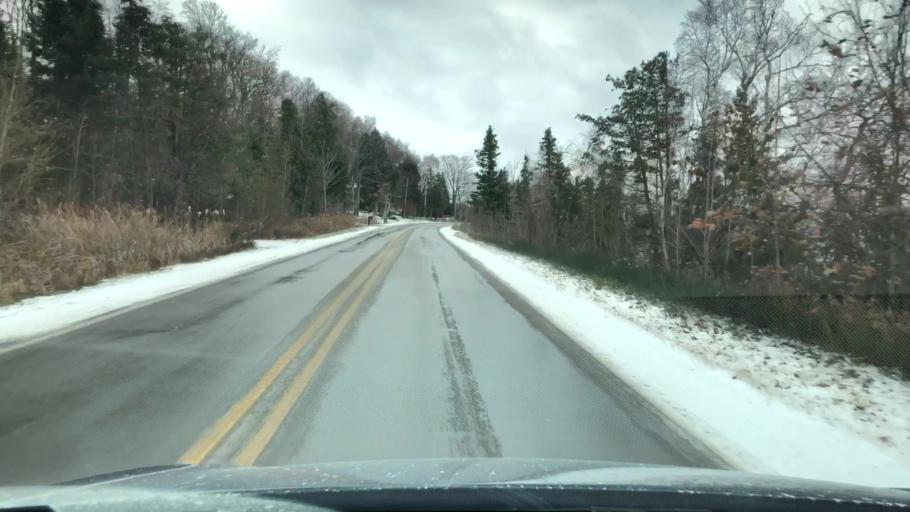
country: US
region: Michigan
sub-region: Leelanau County
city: Greilickville
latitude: 44.8408
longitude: -85.5594
